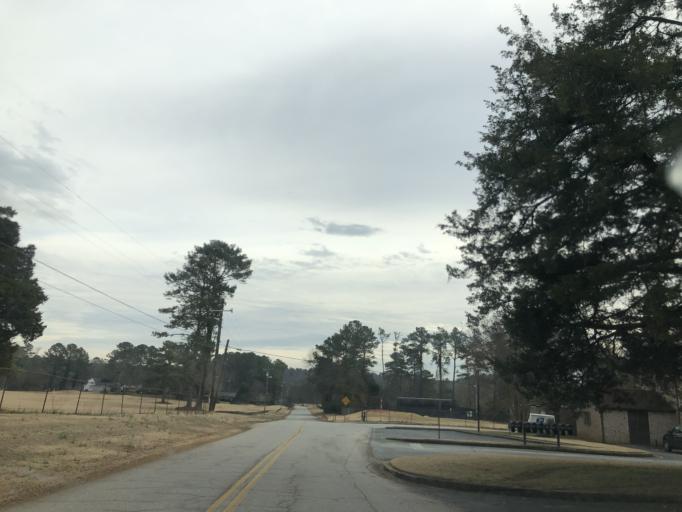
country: US
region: Georgia
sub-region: DeKalb County
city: Pine Mountain
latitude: 33.6404
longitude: -84.1830
